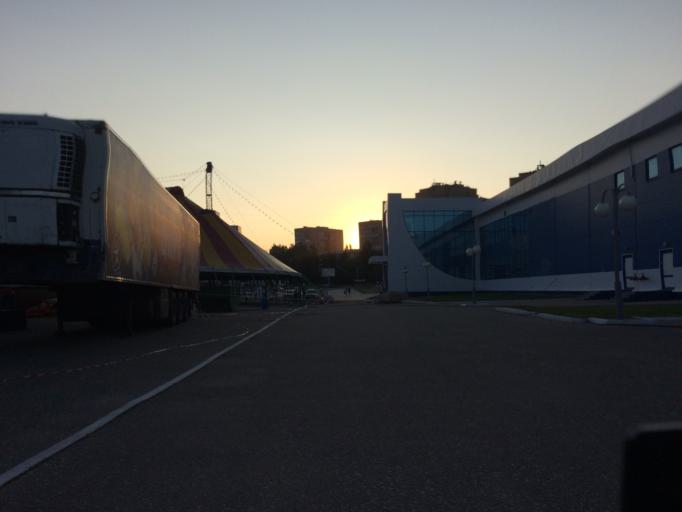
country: RU
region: Mariy-El
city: Yoshkar-Ola
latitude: 56.6238
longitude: 47.8955
